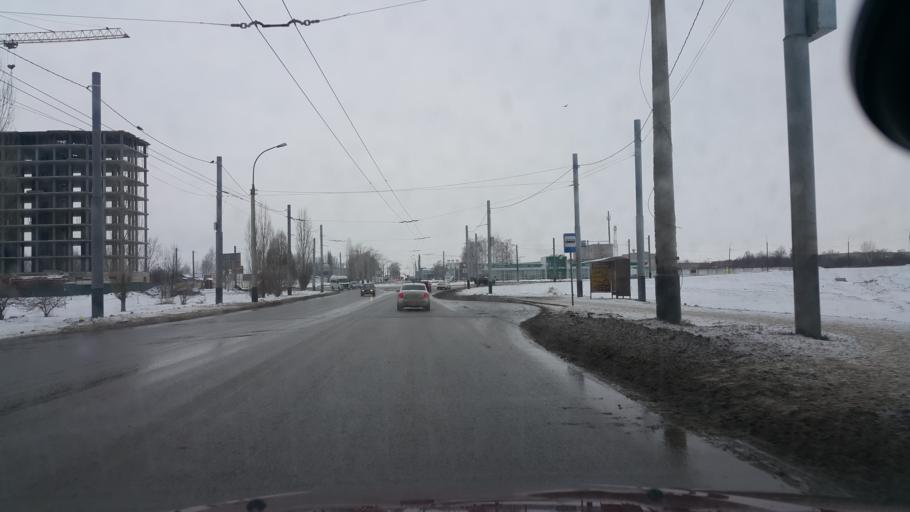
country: RU
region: Tambov
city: Tambov
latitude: 52.7381
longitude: 41.3794
